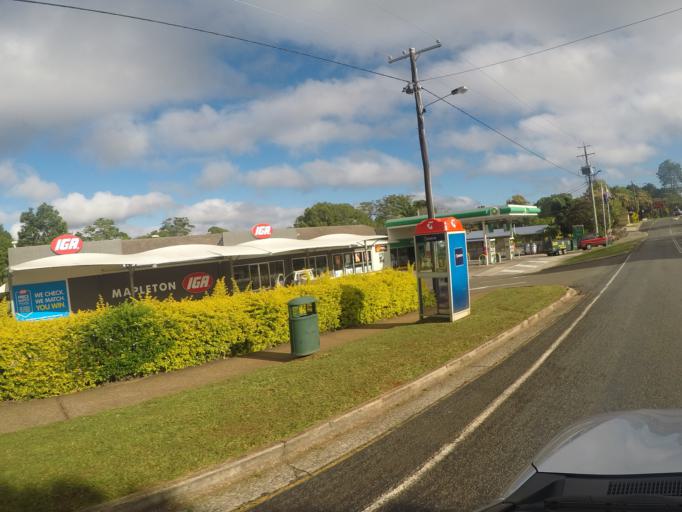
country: AU
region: Queensland
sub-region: Sunshine Coast
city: Nambour
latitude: -26.6269
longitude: 152.8667
